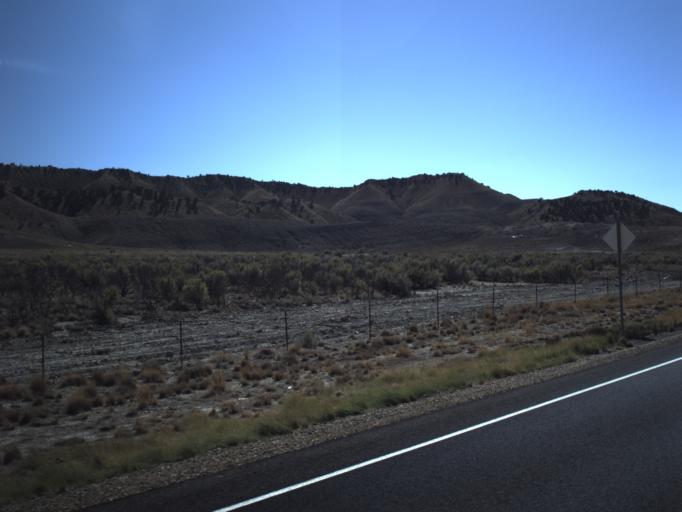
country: US
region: Utah
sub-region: Garfield County
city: Panguitch
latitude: 37.6012
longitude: -111.9693
